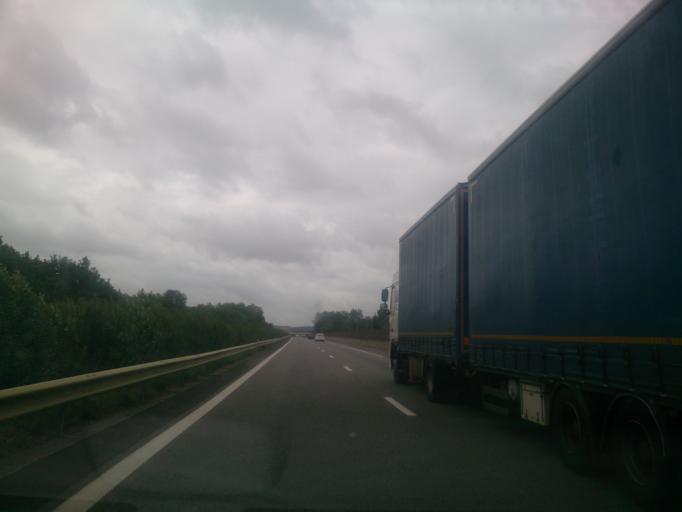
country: FR
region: Midi-Pyrenees
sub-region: Departement de la Haute-Garonne
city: Noe
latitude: 43.3626
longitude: 1.2717
